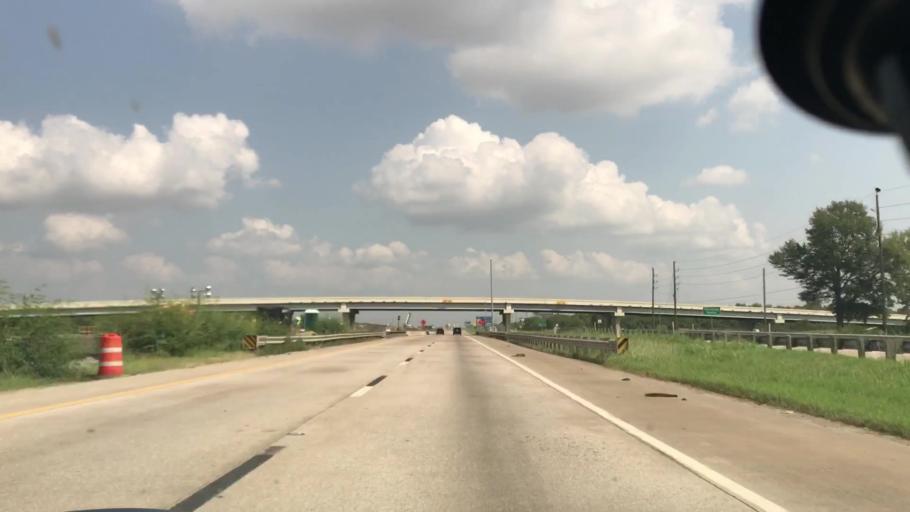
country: US
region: Texas
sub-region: Brazoria County
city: Iowa Colony
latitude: 29.5240
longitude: -95.3866
